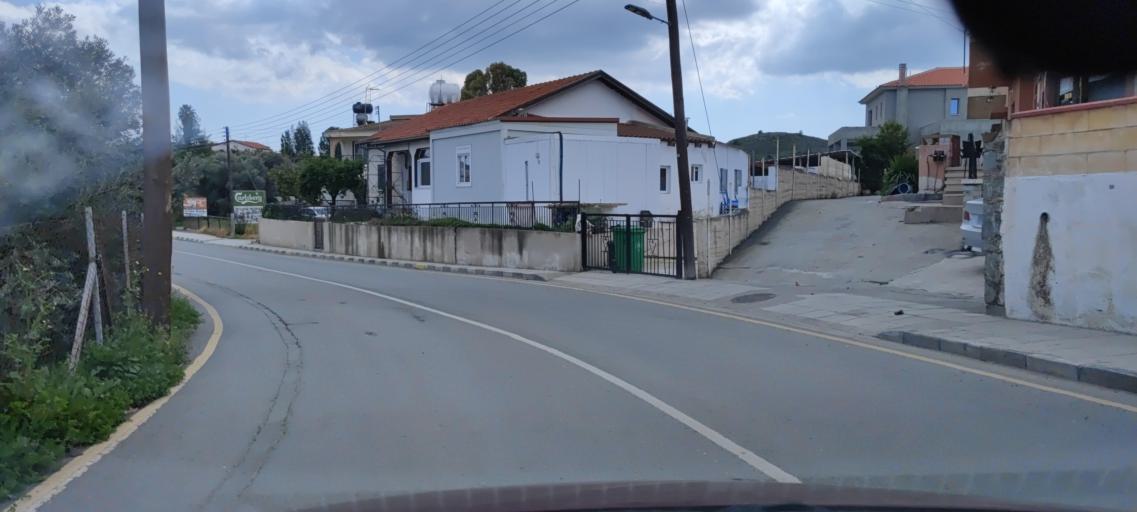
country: CY
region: Larnaka
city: Kornos
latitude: 34.9220
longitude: 33.3967
